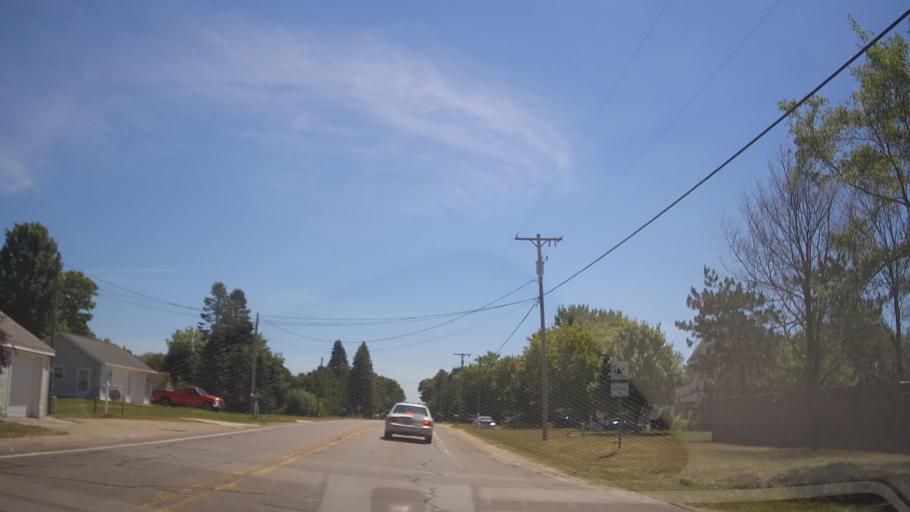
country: US
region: Michigan
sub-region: Grand Traverse County
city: Traverse City
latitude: 44.6942
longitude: -85.6913
